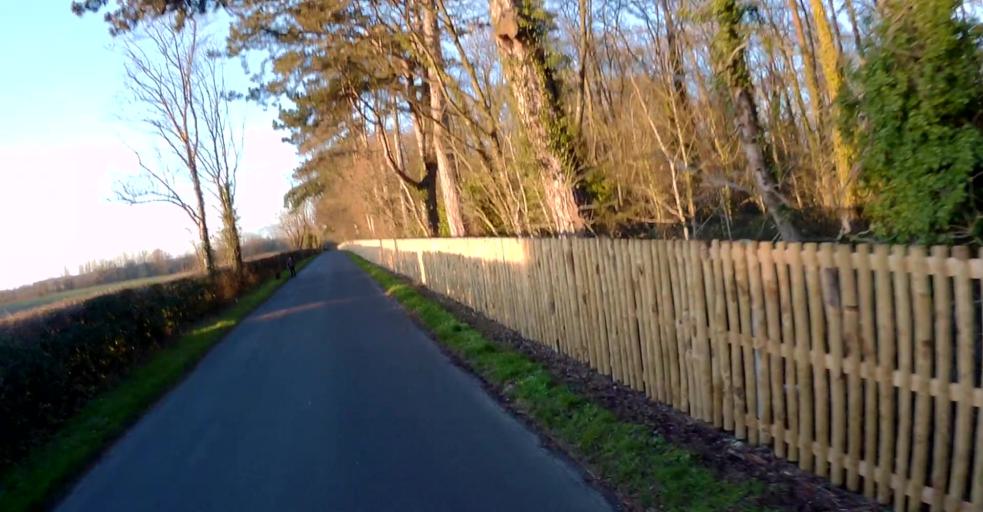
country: GB
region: England
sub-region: West Berkshire
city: Stratfield Mortimer
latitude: 51.3397
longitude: -1.0019
